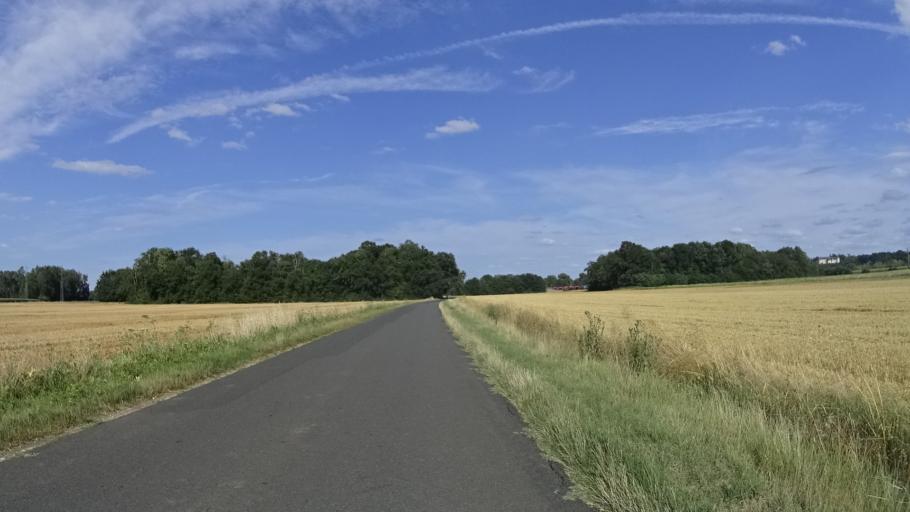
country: FR
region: Centre
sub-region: Departement du Loir-et-Cher
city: Onzain
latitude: 47.4878
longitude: 1.1614
